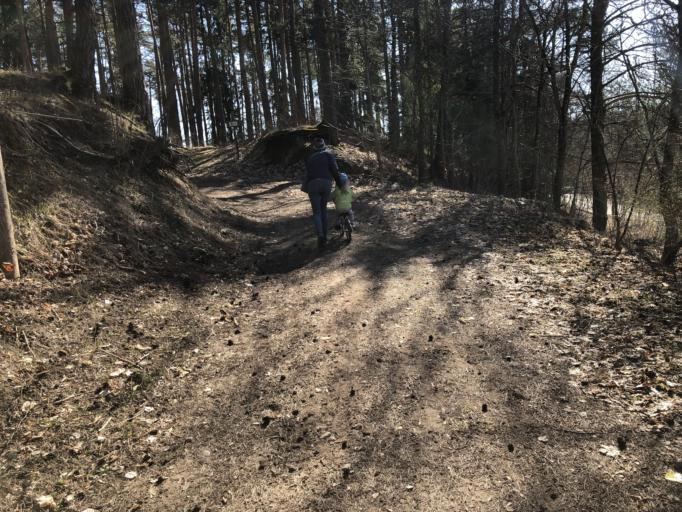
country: EE
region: Harju
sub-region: Kuusalu vald
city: Kuusalu
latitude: 59.2849
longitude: 25.6164
